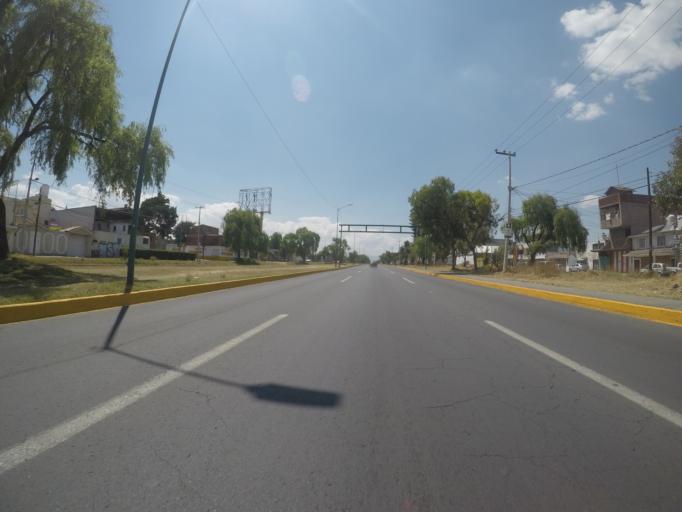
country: MX
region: Mexico
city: San Buenaventura
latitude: 19.2566
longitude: -99.6645
